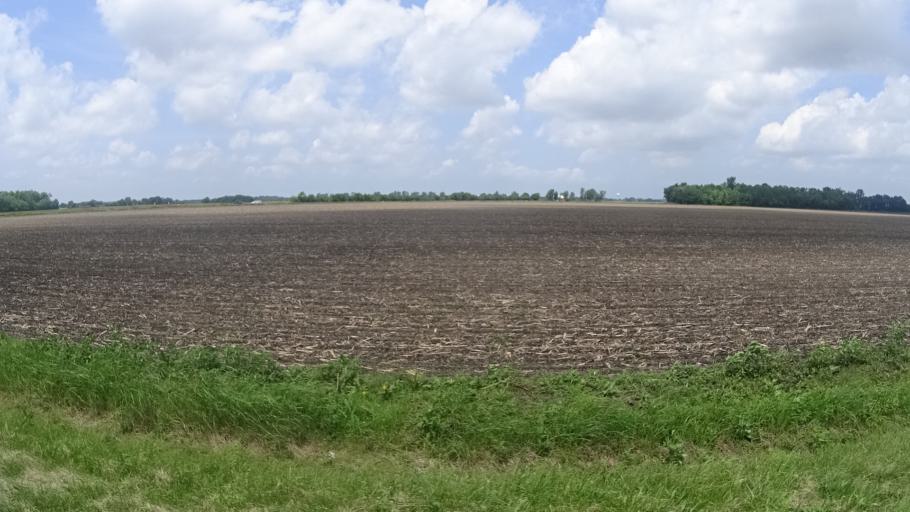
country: US
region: Ohio
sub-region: Huron County
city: Bellevue
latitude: 41.2983
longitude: -82.7764
